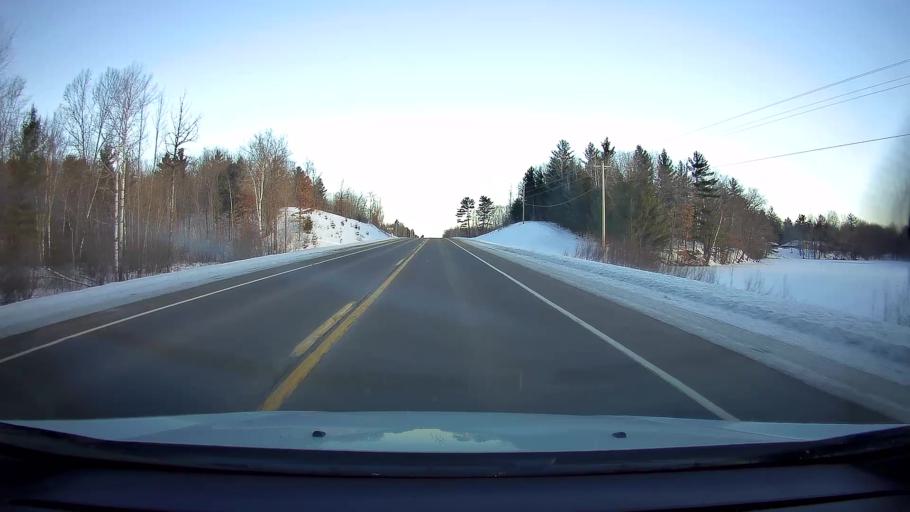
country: US
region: Wisconsin
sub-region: Barron County
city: Cumberland
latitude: 45.5829
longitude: -92.0176
